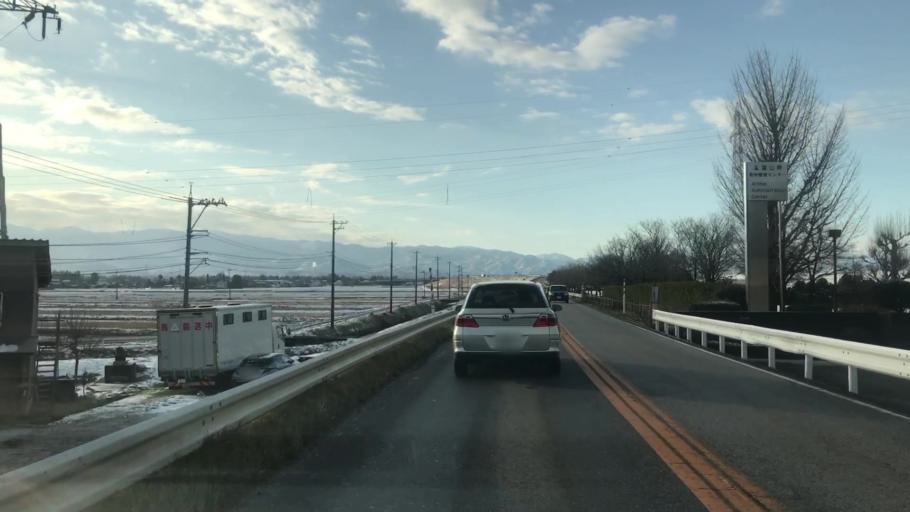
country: JP
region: Toyama
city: Toyama-shi
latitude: 36.6844
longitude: 137.2845
